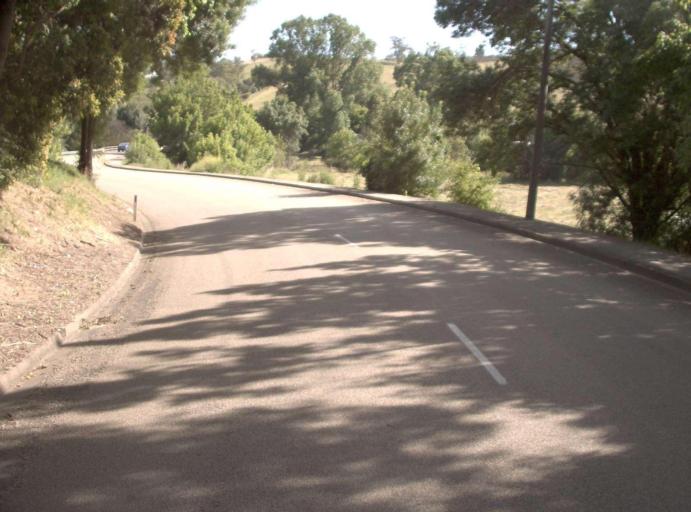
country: AU
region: Victoria
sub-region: East Gippsland
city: Lakes Entrance
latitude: -37.4982
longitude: 148.1729
